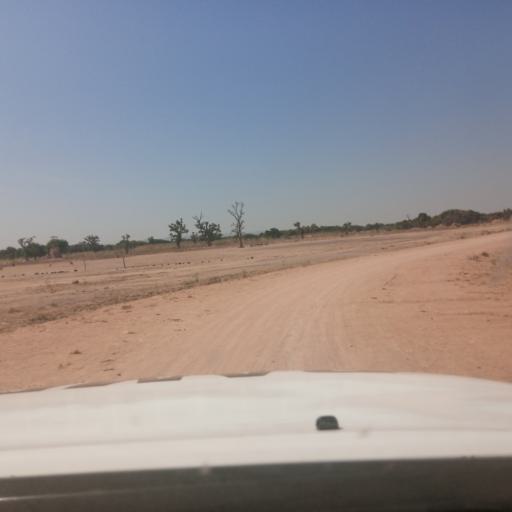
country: NG
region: Adamawa
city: Little Gombi
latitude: 9.7755
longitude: 12.5875
